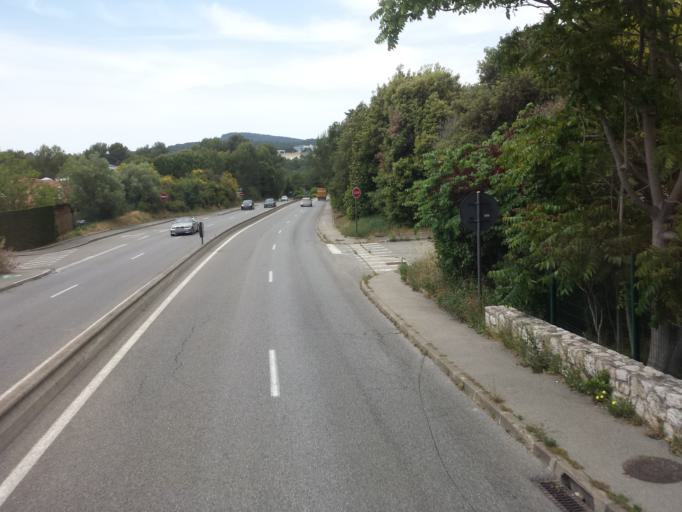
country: FR
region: Provence-Alpes-Cote d'Azur
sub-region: Departement des Alpes-Maritimes
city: Biot
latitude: 43.6141
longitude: 7.0800
